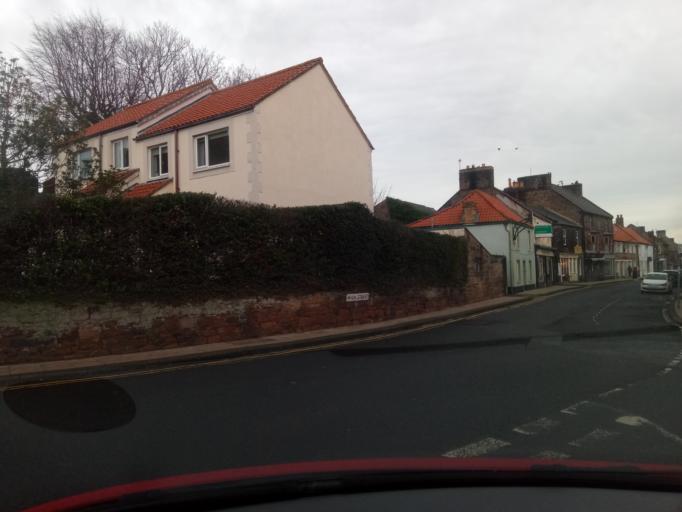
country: GB
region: England
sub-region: Northumberland
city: Wooler
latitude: 55.5473
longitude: -2.0178
